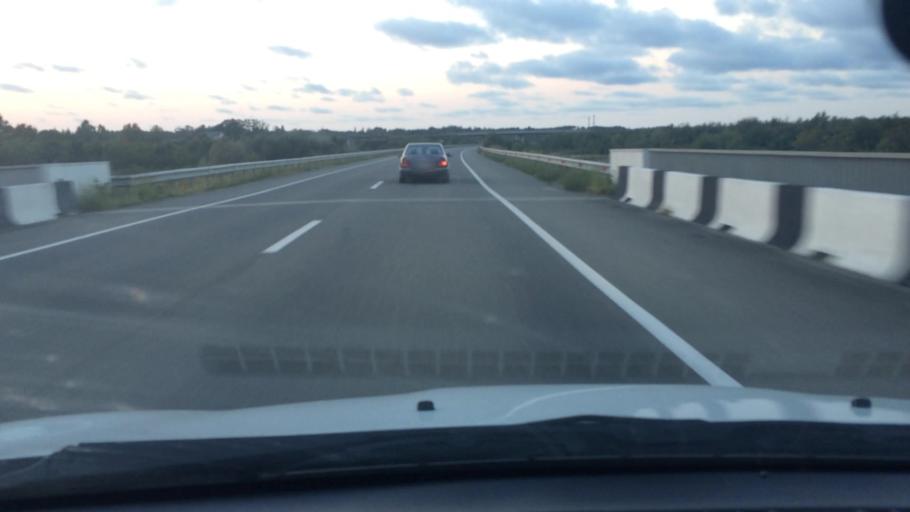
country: GE
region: Guria
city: Urek'i
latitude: 41.9137
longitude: 41.7791
